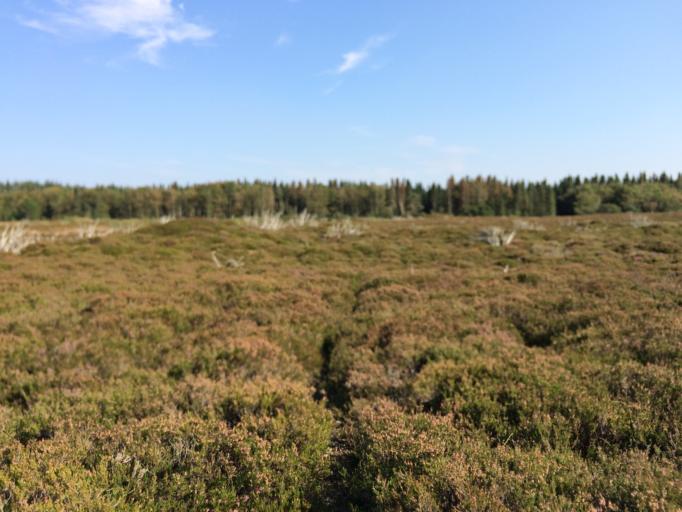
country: DK
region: Central Jutland
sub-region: Holstebro Kommune
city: Ulfborg
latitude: 56.2558
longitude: 8.4228
